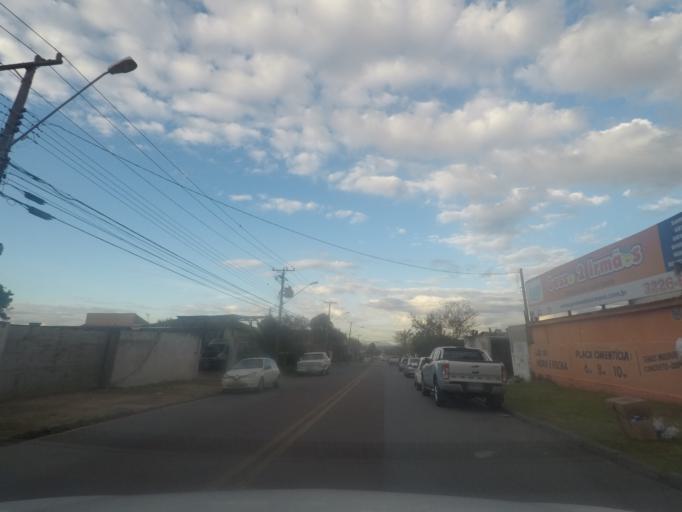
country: BR
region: Parana
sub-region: Pinhais
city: Pinhais
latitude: -25.4684
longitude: -49.2103
